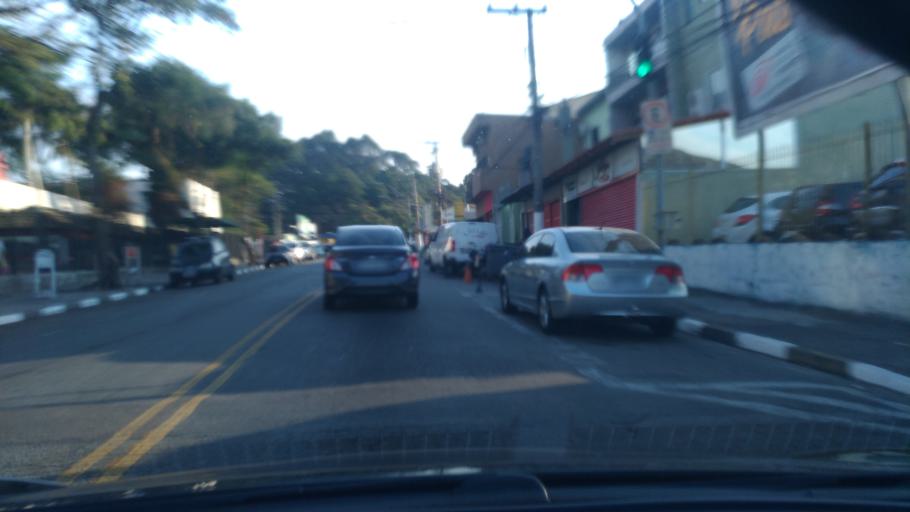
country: BR
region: Sao Paulo
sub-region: Osasco
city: Osasco
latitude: -23.5349
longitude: -46.7917
